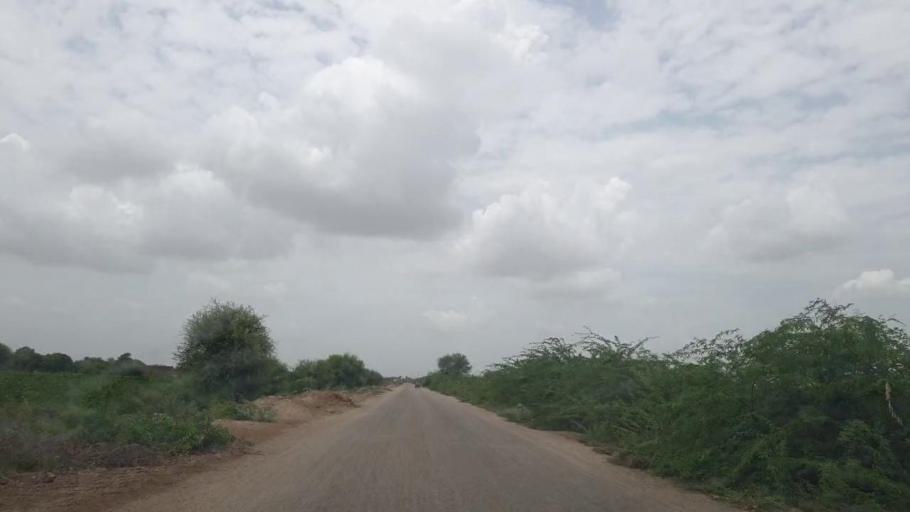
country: PK
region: Sindh
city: Naukot
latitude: 24.9233
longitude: 69.2739
